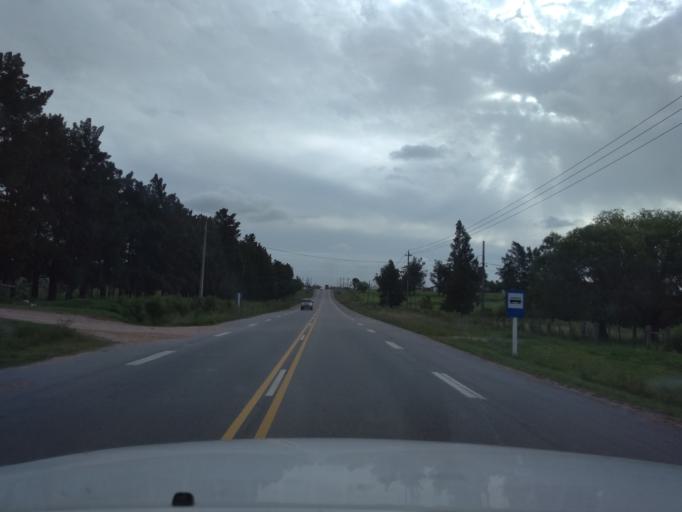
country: UY
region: Canelones
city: Joaquin Suarez
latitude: -34.7060
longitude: -56.0482
